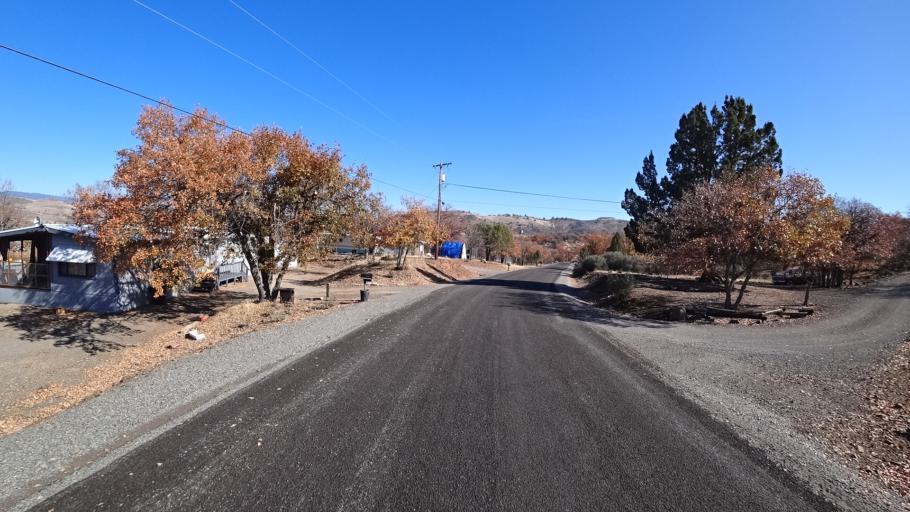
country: US
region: California
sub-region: Siskiyou County
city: Montague
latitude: 41.8828
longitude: -122.4889
